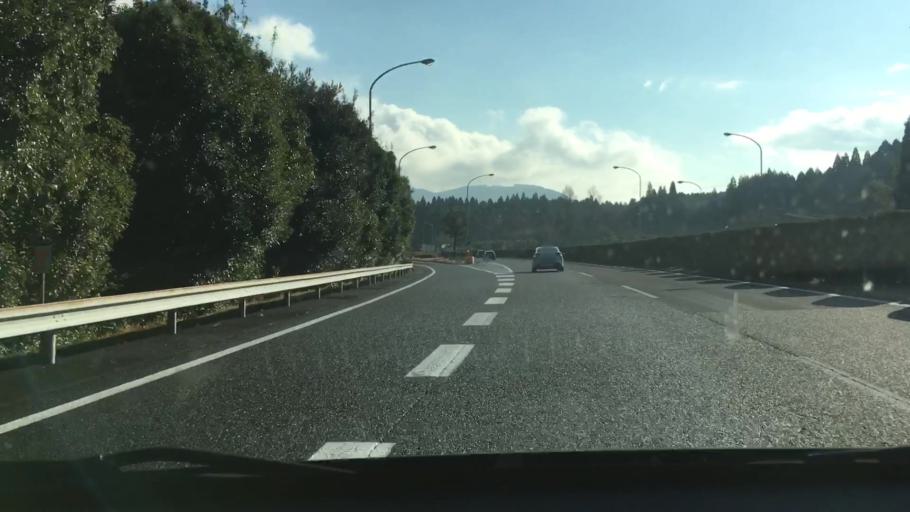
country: JP
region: Kagoshima
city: Okuchi-shinohara
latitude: 32.0082
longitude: 130.7558
